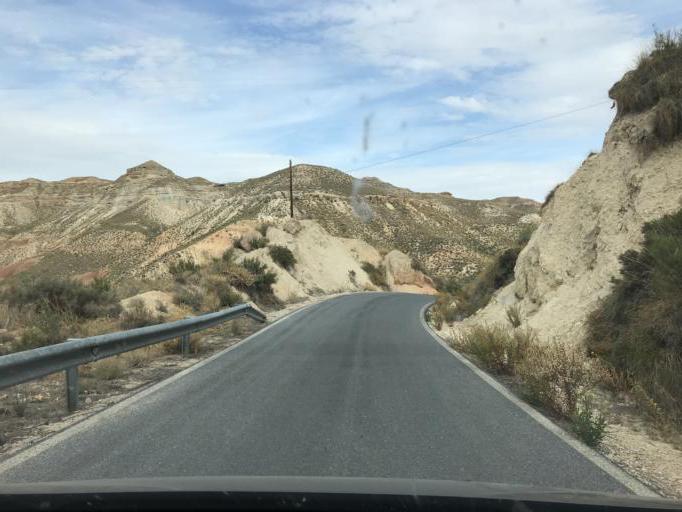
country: ES
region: Andalusia
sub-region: Provincia de Granada
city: Villanueva de las Torres
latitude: 37.5018
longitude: -3.0864
